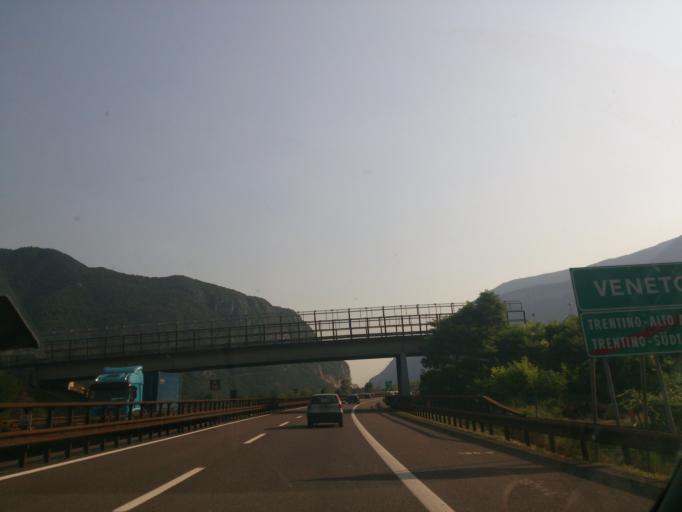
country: IT
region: Trentino-Alto Adige
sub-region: Provincia di Trento
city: Avio
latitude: 45.6998
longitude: 10.9213
